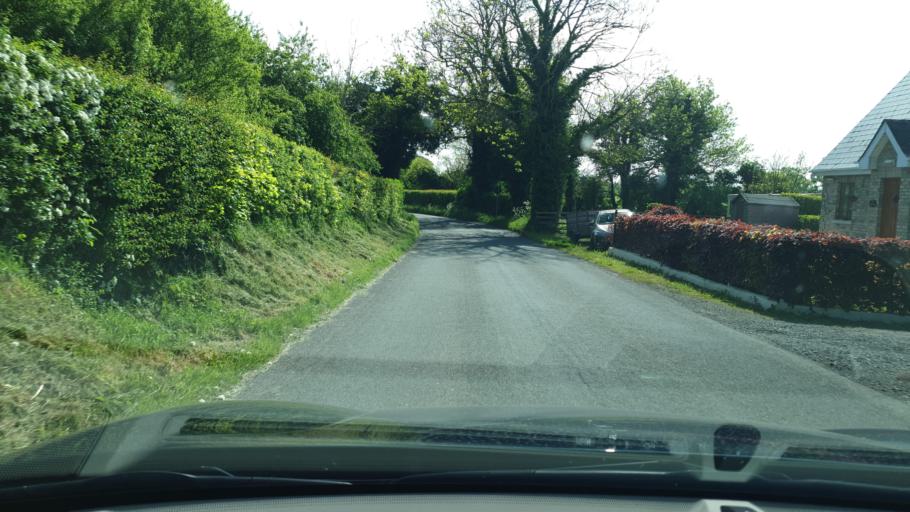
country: IE
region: Leinster
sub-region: Kildare
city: Maynooth
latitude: 53.4084
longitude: -6.5771
